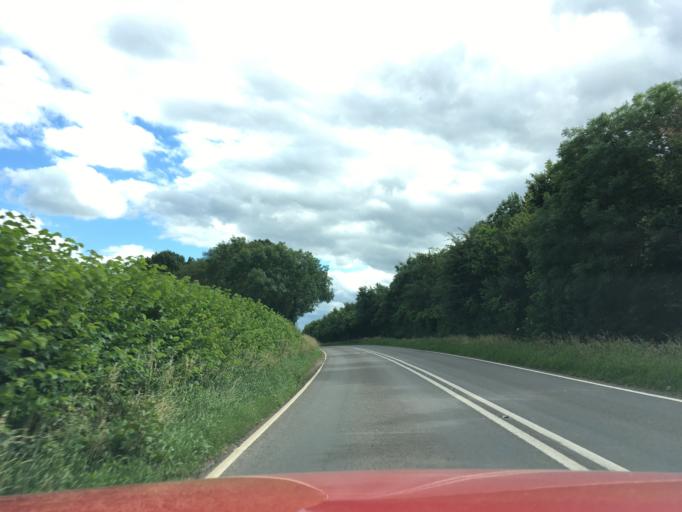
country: GB
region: England
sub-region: Leicestershire
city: Measham
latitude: 52.6658
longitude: -1.5388
